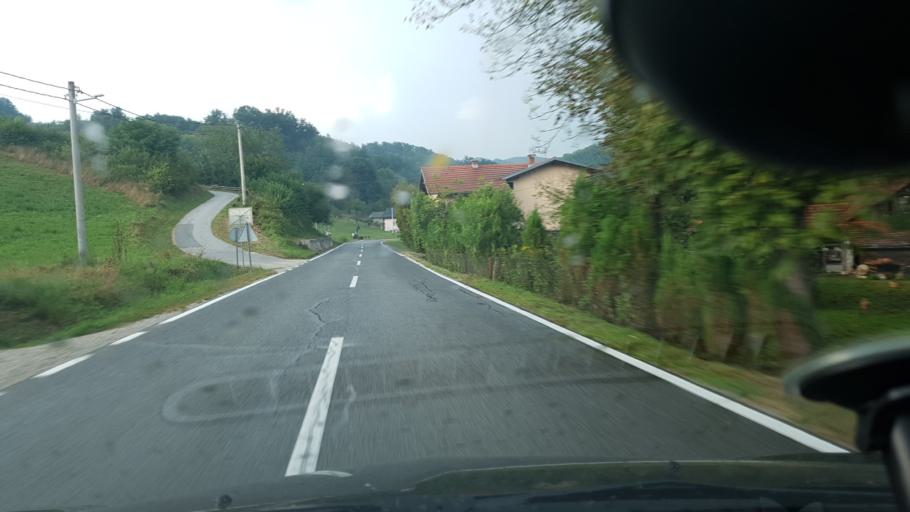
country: HR
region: Krapinsko-Zagorska
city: Pregrada
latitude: 46.2103
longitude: 15.7495
